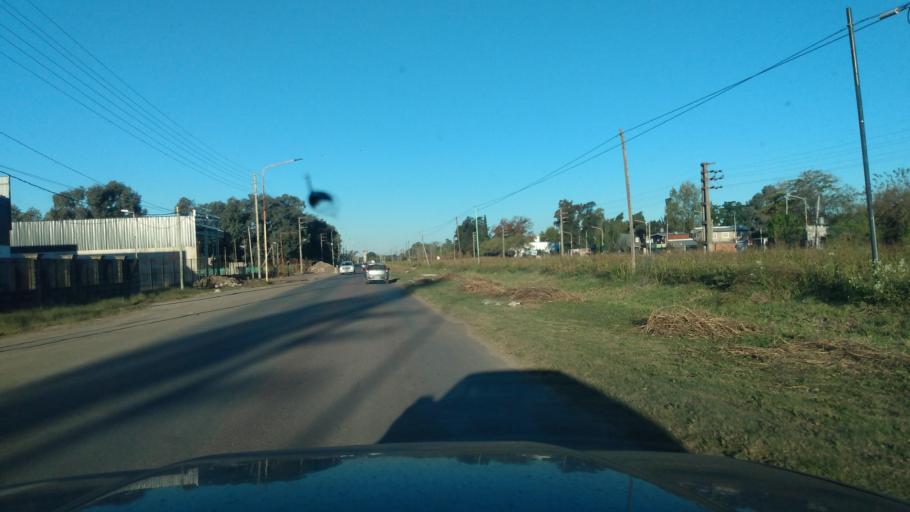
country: AR
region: Buenos Aires
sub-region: Partido de General Rodriguez
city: General Rodriguez
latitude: -34.6263
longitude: -58.8773
